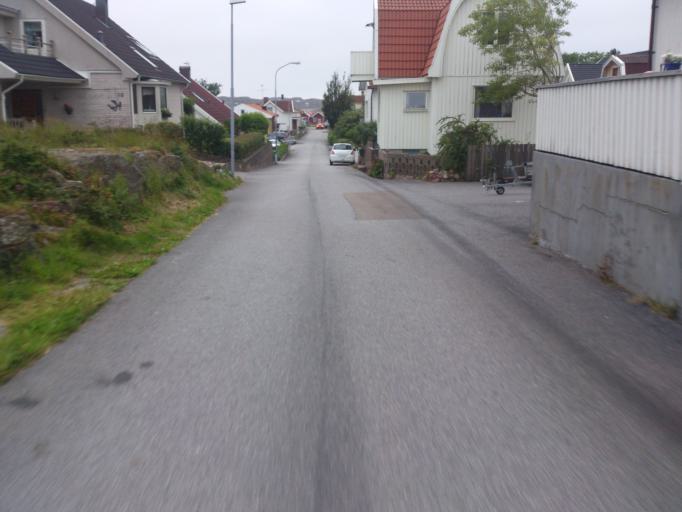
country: SE
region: Vaestra Goetaland
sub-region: Sotenas Kommun
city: Kungshamn
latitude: 58.3815
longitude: 11.2671
